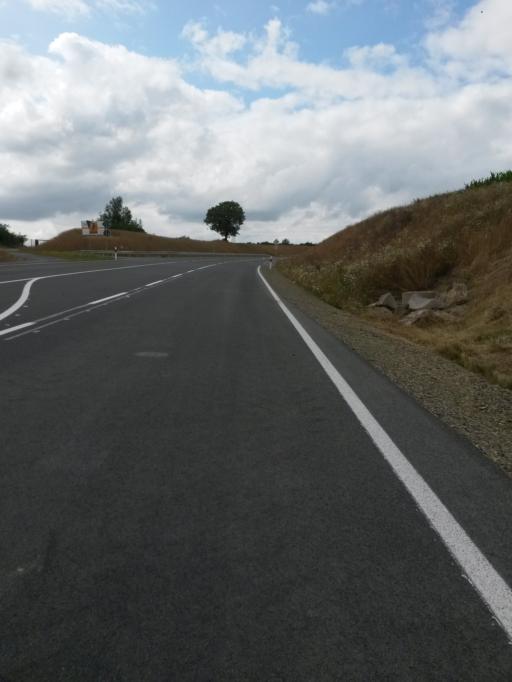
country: DE
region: North Rhine-Westphalia
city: Bad Oeynhausen
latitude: 52.1473
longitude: 8.7772
